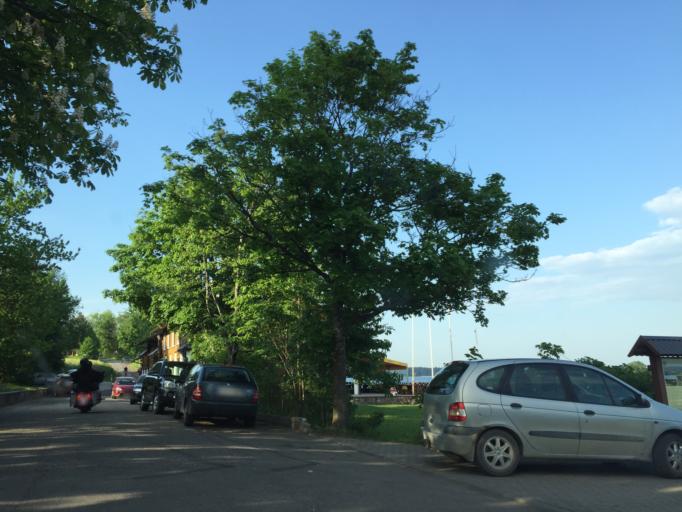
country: LT
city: Plateliai
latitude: 56.0471
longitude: 21.8313
